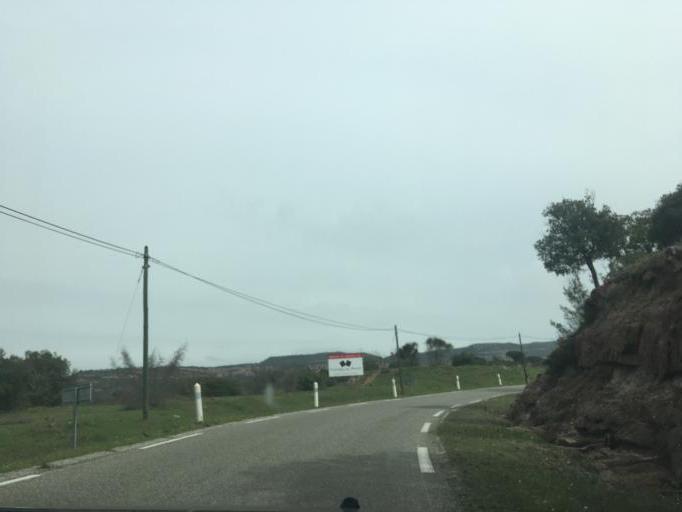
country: FR
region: Provence-Alpes-Cote d'Azur
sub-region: Departement du Var
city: Le Muy
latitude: 43.5043
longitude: 6.5915
